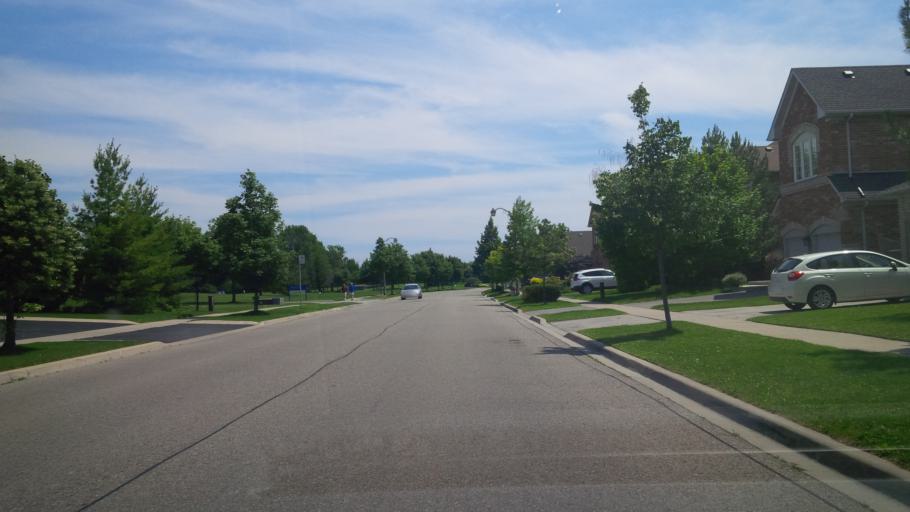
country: CA
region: Ontario
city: Burlington
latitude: 43.3961
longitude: -79.8017
